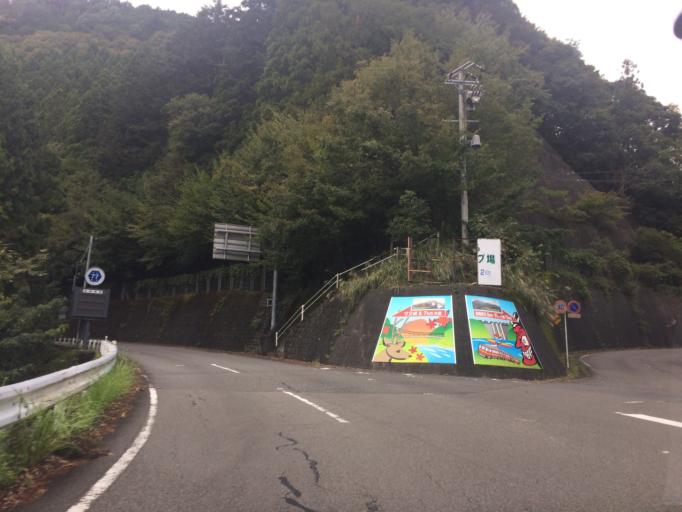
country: JP
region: Shizuoka
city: Shizuoka-shi
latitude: 35.1541
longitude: 138.1442
